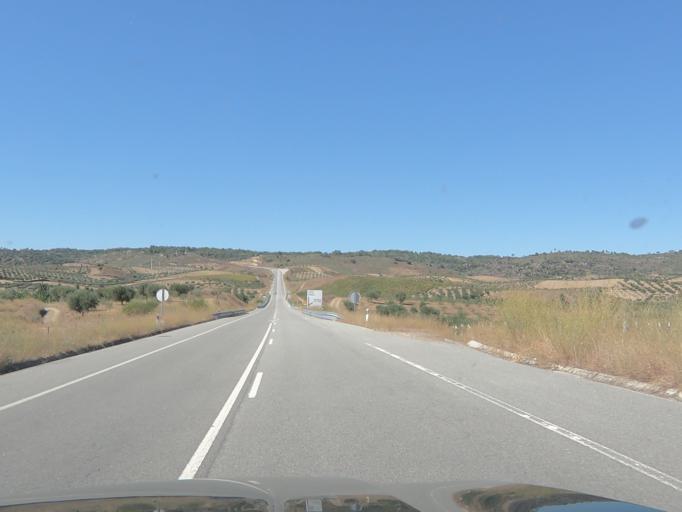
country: PT
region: Vila Real
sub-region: Valpacos
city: Valpacos
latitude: 41.5567
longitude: -7.2613
